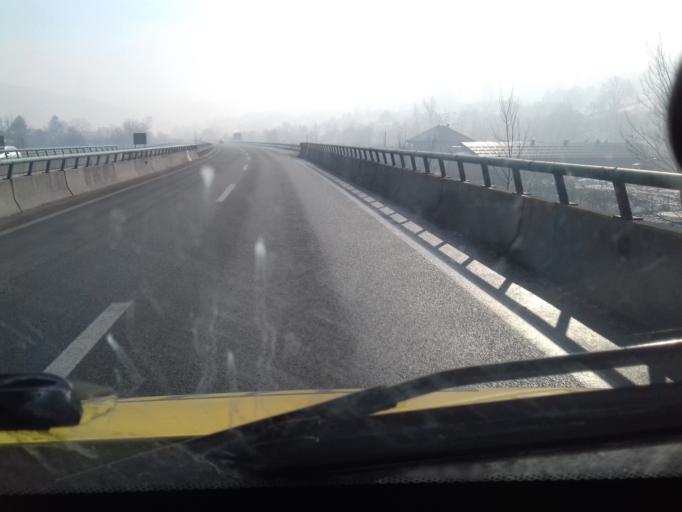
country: BA
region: Federation of Bosnia and Herzegovina
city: Vogosca
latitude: 43.9235
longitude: 18.3060
